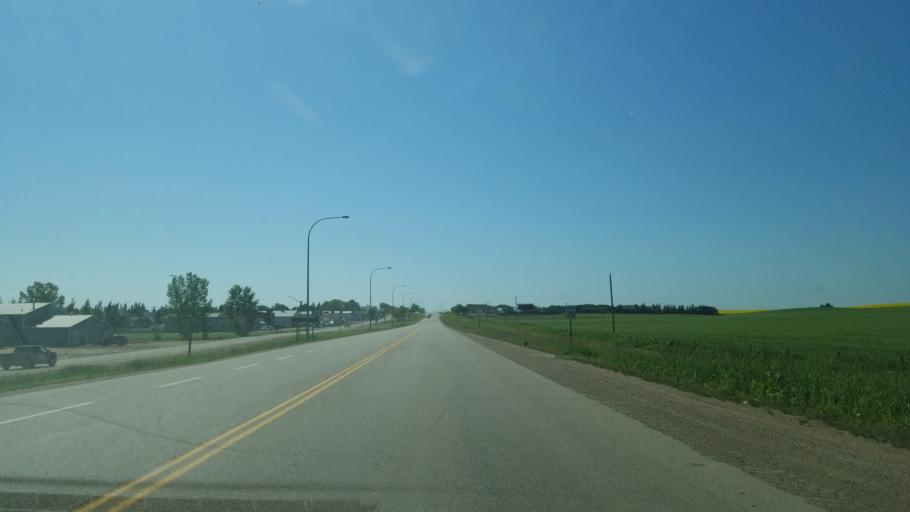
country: CA
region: Alberta
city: Provost
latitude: 52.3612
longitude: -110.2460
